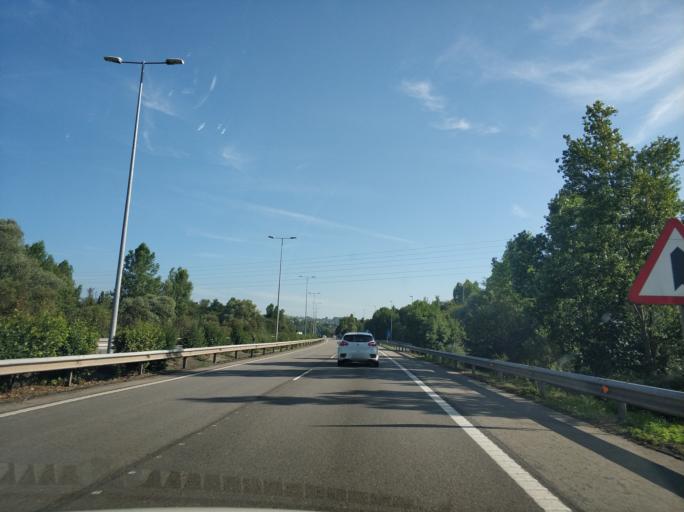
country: ES
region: Asturias
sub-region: Province of Asturias
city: Lugones
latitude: 43.3807
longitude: -5.8127
